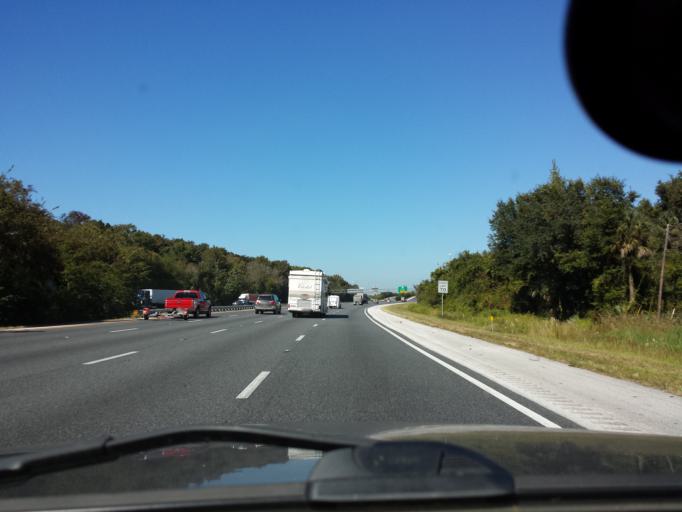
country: US
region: Florida
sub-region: Sumter County
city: Wildwood
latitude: 28.8650
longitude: -82.0914
